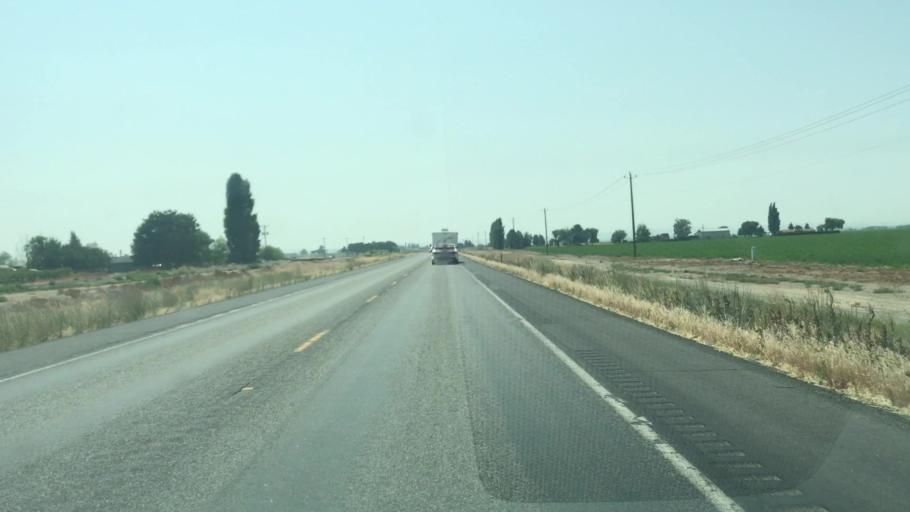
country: US
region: Washington
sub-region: Grant County
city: Quincy
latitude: 47.1518
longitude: -119.8536
